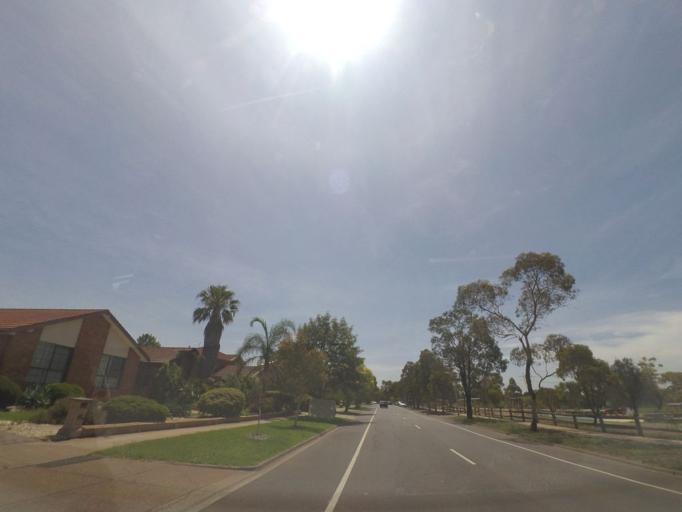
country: AU
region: Victoria
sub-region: Brimbank
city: Taylors Lakes
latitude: -37.7046
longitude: 144.7943
